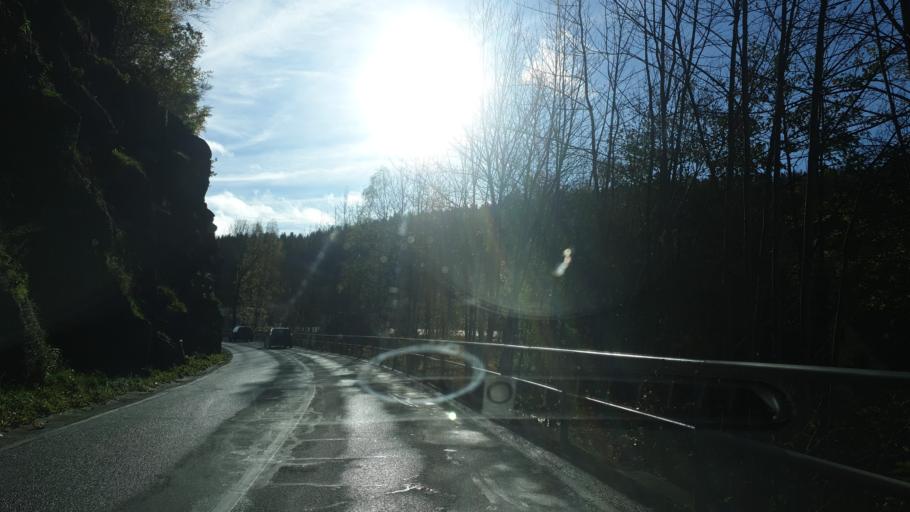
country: DE
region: Saxony
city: Aue
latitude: 50.5790
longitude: 12.6890
